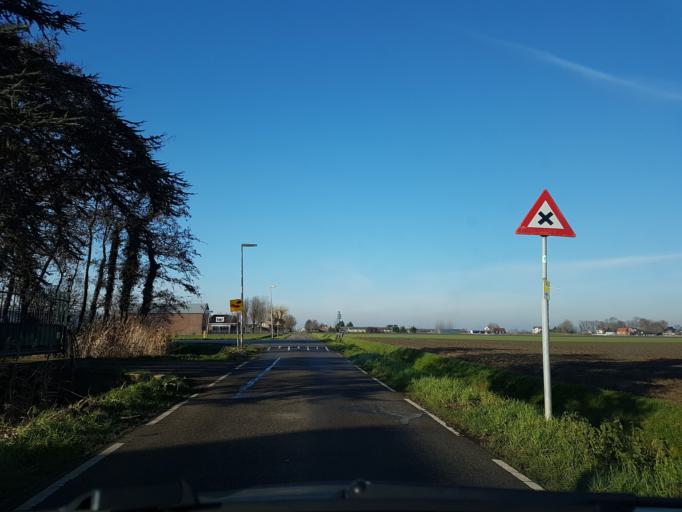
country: NL
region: South Holland
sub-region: Gemeente Waddinxveen
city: Groenswaard
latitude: 52.0420
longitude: 4.6126
